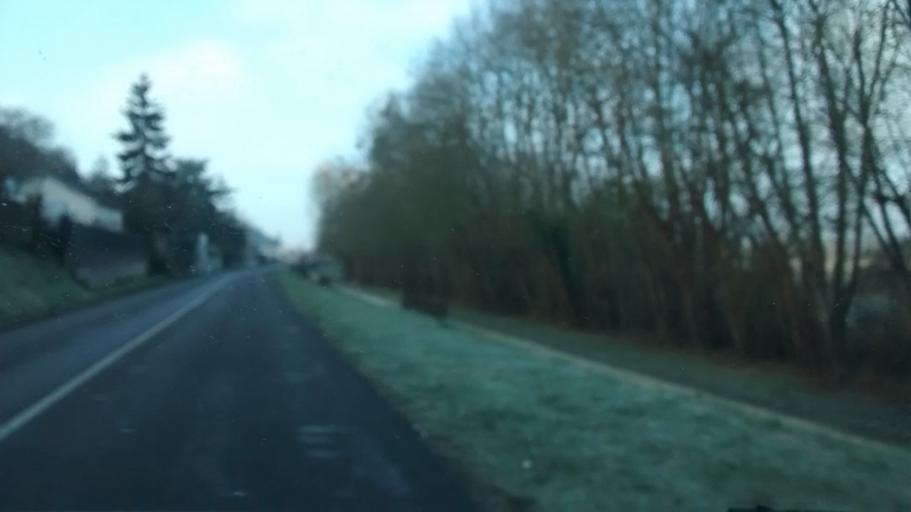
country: FR
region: Centre
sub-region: Departement d'Indre-et-Loire
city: Savonnieres
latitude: 47.3497
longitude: 0.5574
